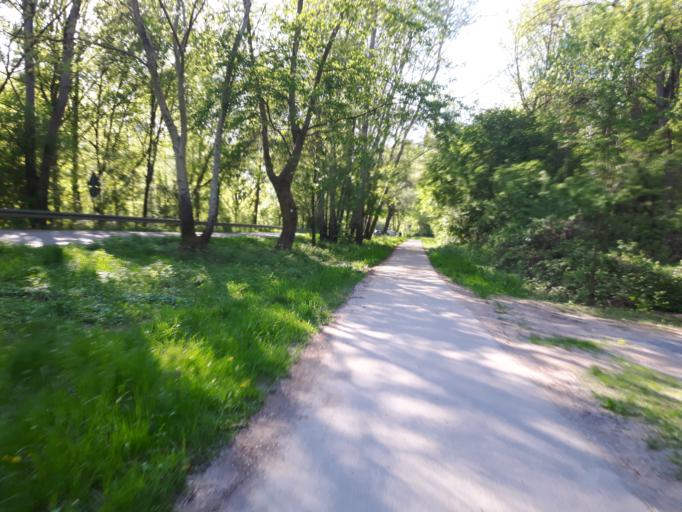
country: DE
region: Baden-Wuerttemberg
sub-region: Karlsruhe Region
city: Bruhl
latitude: 49.3889
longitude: 8.5080
